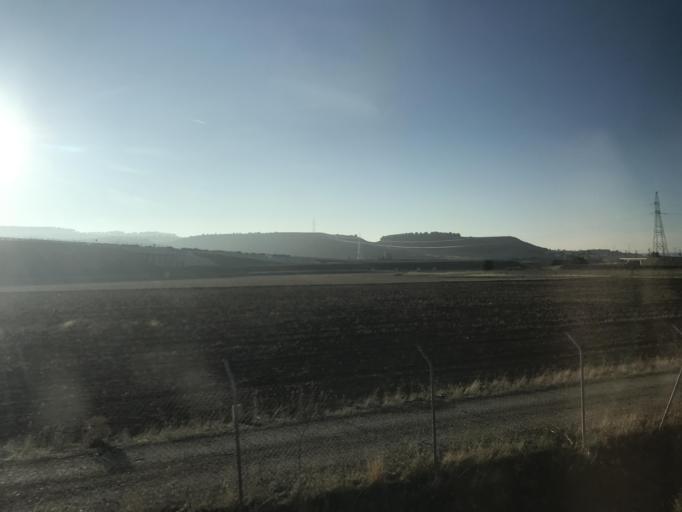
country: ES
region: Castille and Leon
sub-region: Provincia de Valladolid
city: Santovenia de Pisuerga
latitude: 41.7032
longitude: -4.6742
